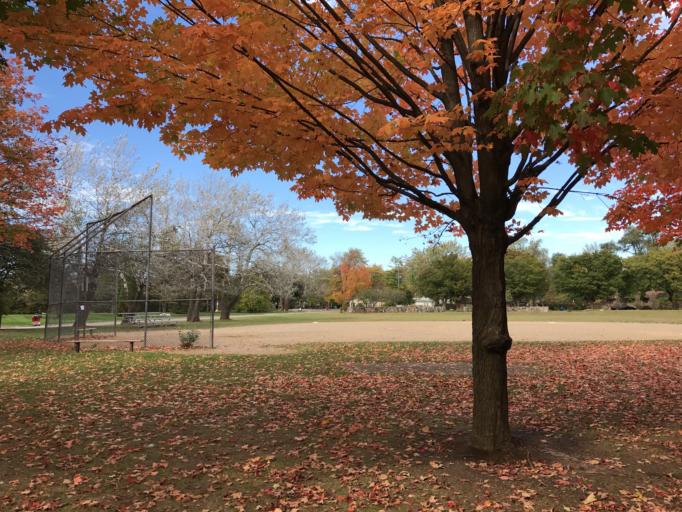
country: US
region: Michigan
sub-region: Washtenaw County
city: Ann Arbor
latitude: 42.2595
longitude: -83.7351
